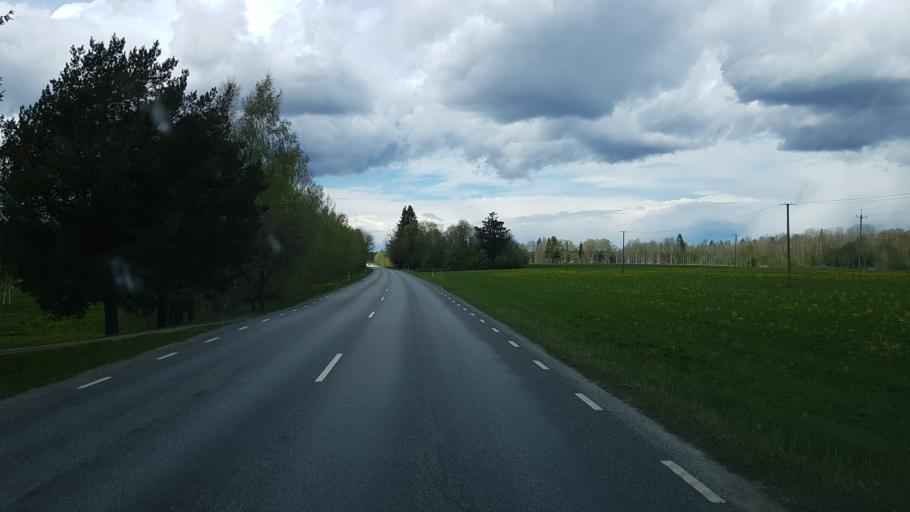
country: EE
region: Laeaene
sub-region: Lihula vald
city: Lihula
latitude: 58.5234
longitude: 24.0724
